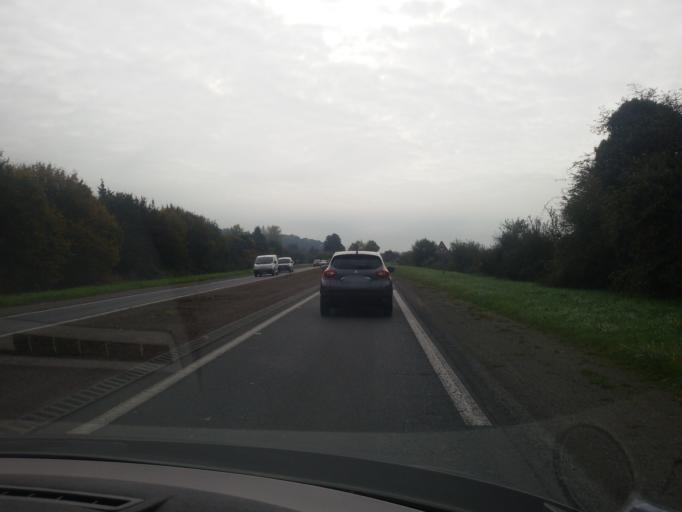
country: FR
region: Lower Normandy
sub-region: Departement du Calvados
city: Dives-sur-Mer
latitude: 49.2601
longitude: -0.1042
